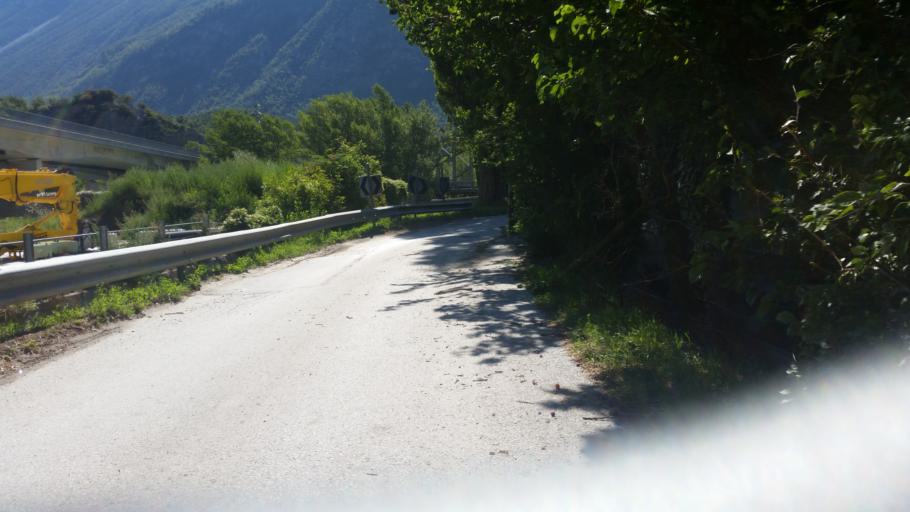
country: CH
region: Valais
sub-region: Sierre District
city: Chippis
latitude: 46.2956
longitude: 7.5530
